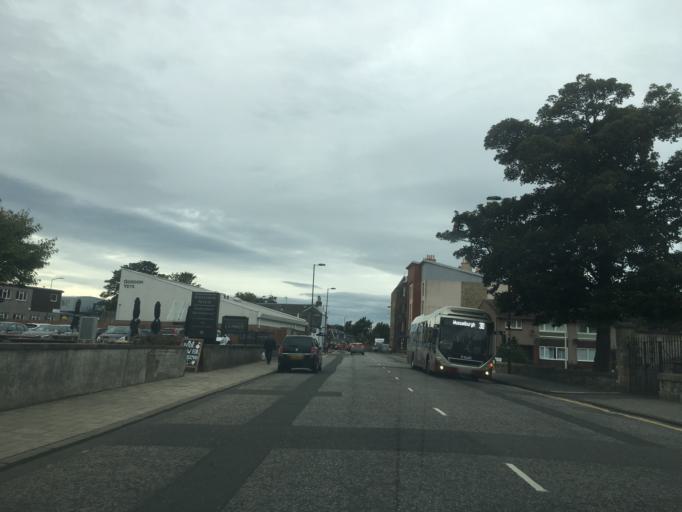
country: GB
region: Scotland
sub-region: East Lothian
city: Musselburgh
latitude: 55.9439
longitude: -3.0643
